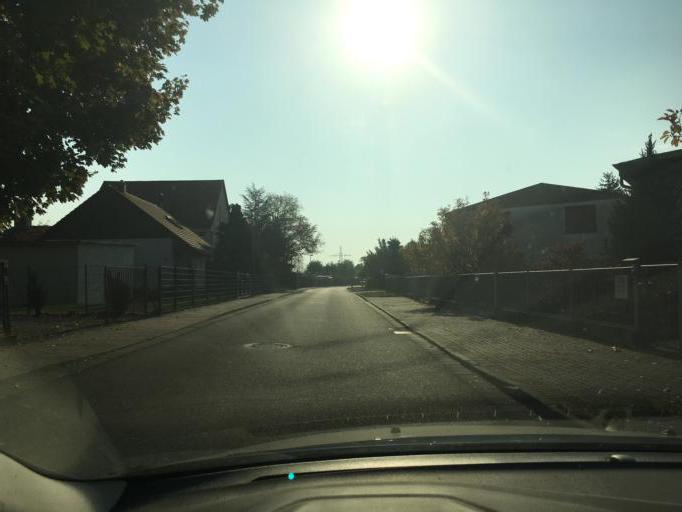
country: DE
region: Saxony
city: Wurzen
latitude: 51.3607
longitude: 12.7419
